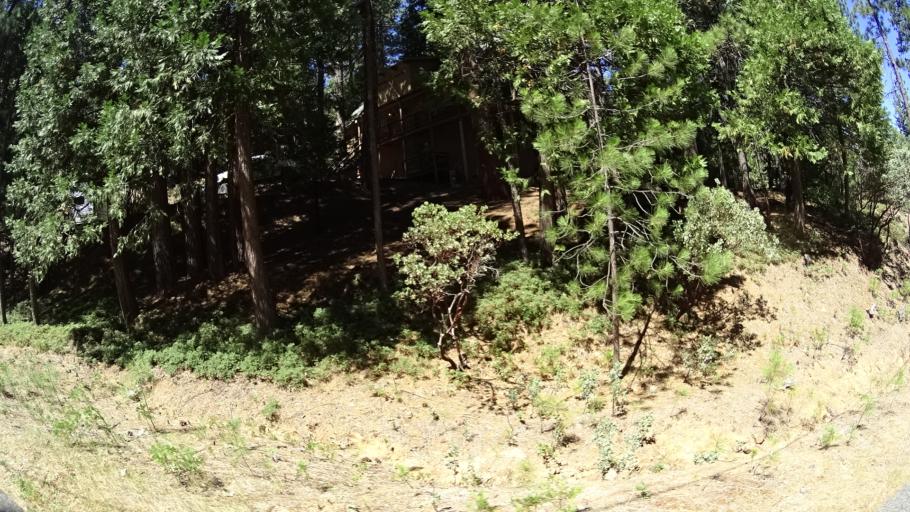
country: US
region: California
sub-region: Calaveras County
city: Arnold
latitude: 38.2275
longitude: -120.3434
